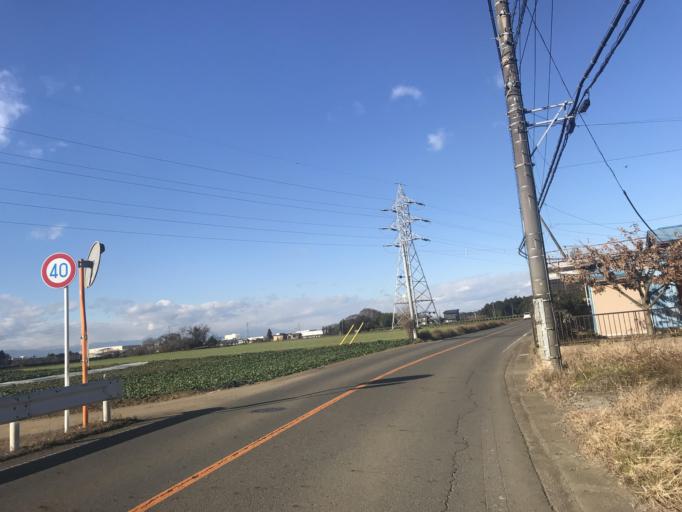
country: JP
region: Tochigi
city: Kaminokawa
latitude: 36.4093
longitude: 139.8771
